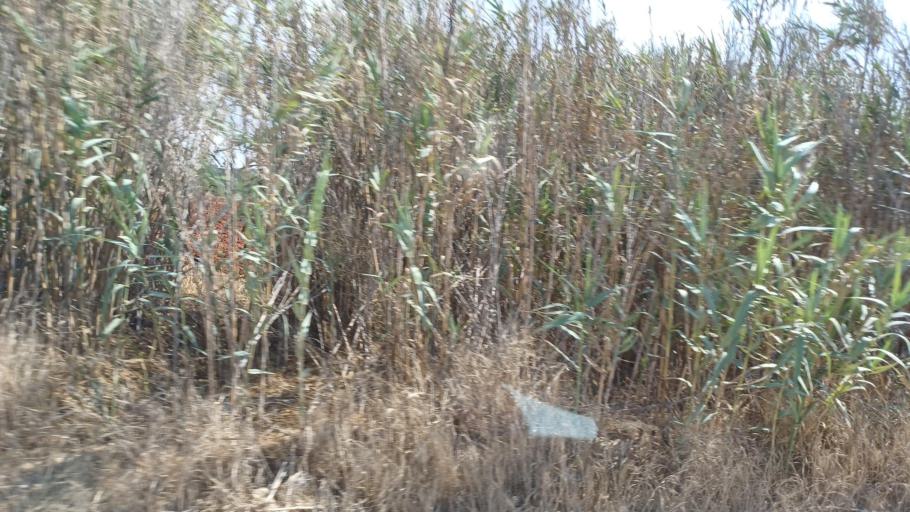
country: CY
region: Larnaka
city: Xylotymbou
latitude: 34.9766
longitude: 33.7897
